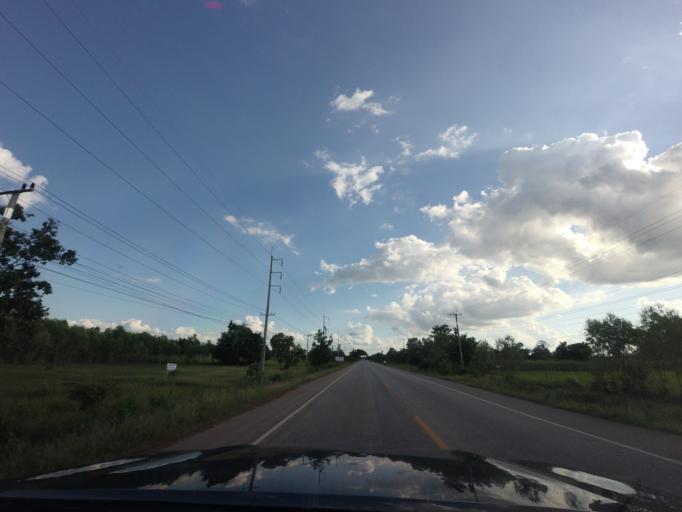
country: TH
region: Changwat Udon Thani
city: Thung Fon
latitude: 17.4769
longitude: 103.1946
